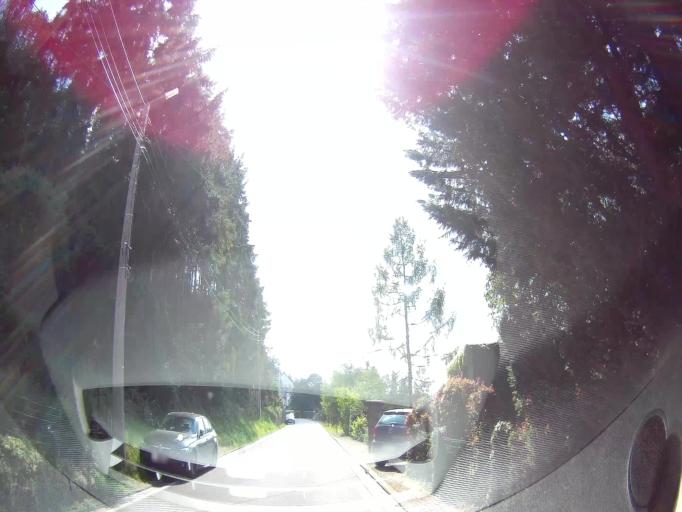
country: BE
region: Wallonia
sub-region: Province de Namur
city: Yvoir
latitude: 50.3511
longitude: 4.8809
